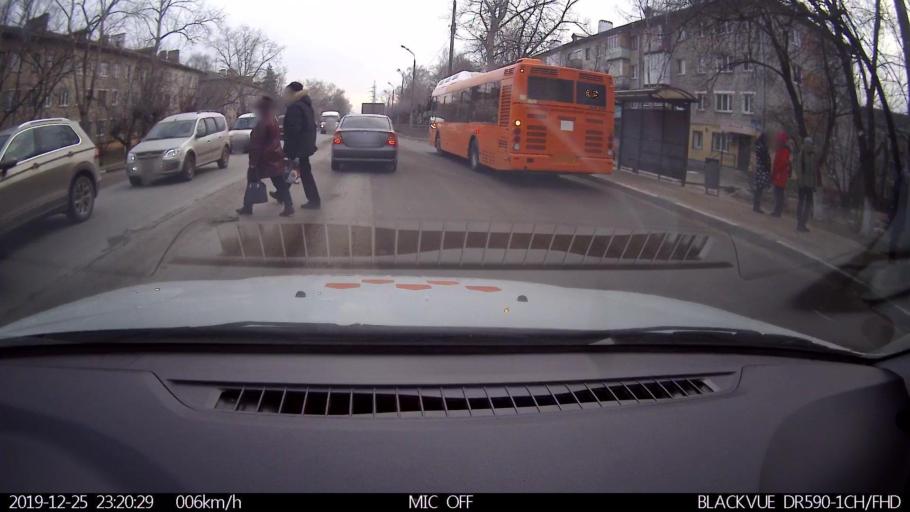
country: RU
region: Nizjnij Novgorod
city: Gorbatovka
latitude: 56.3535
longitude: 43.8327
